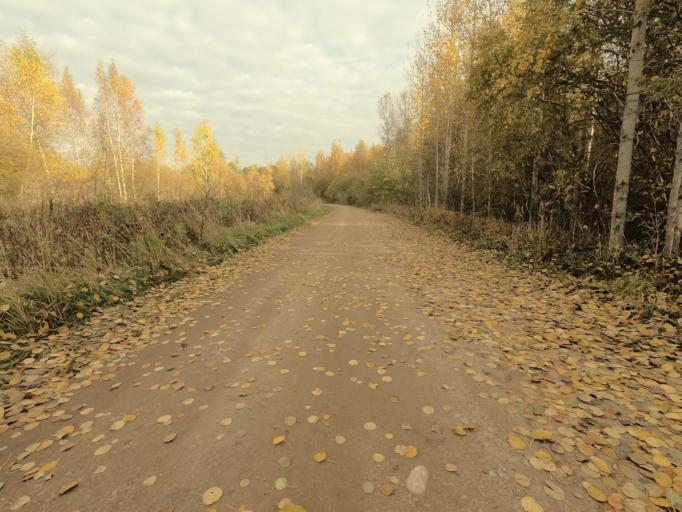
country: RU
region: Novgorod
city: Volkhovskiy
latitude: 58.8929
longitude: 31.0250
